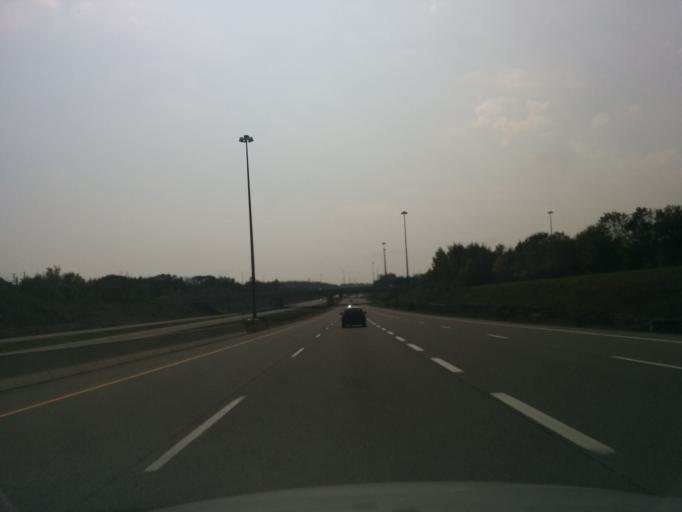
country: CA
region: Ontario
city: Bells Corners
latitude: 45.3383
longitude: -75.8144
